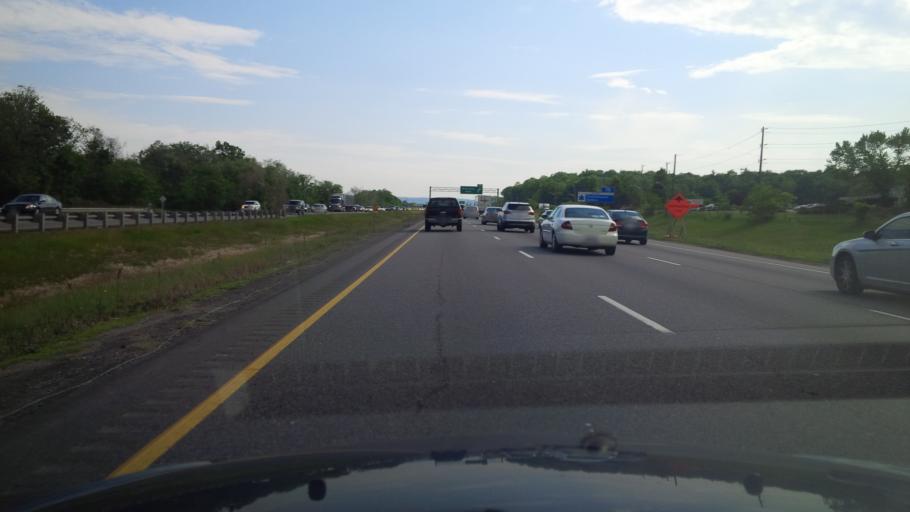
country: CA
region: Ontario
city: Burlington
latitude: 43.3196
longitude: -79.8523
